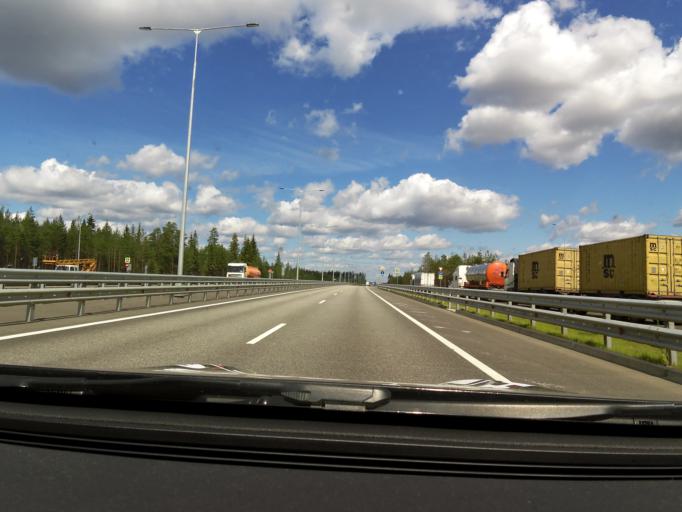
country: RU
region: Tverskaya
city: Krasnomayskiy
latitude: 57.5284
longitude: 34.2761
